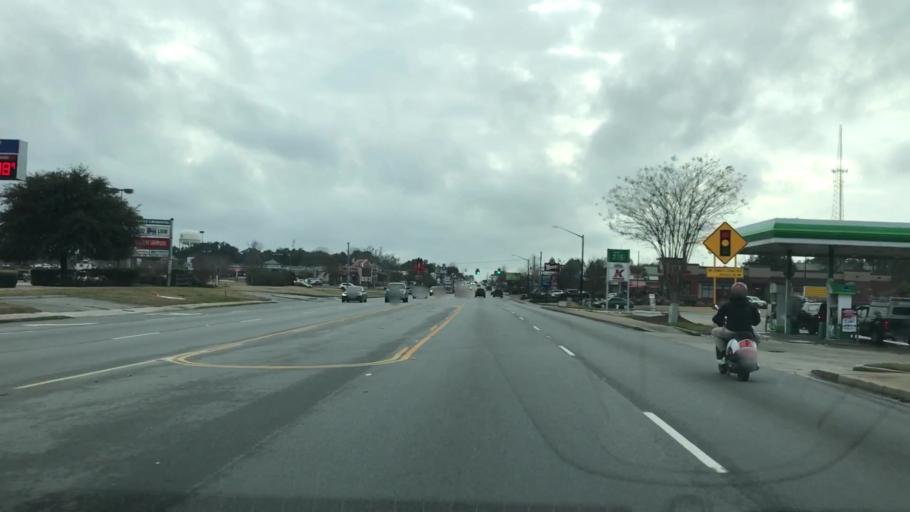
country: US
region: South Carolina
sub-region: Berkeley County
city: Moncks Corner
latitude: 33.2108
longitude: -79.9806
